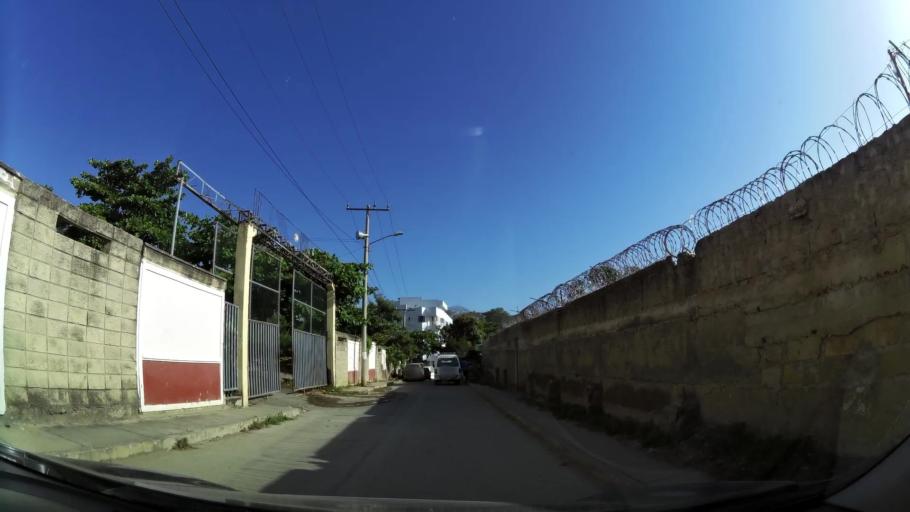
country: CO
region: Bolivar
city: Cartagena
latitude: 10.4016
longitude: -75.5046
